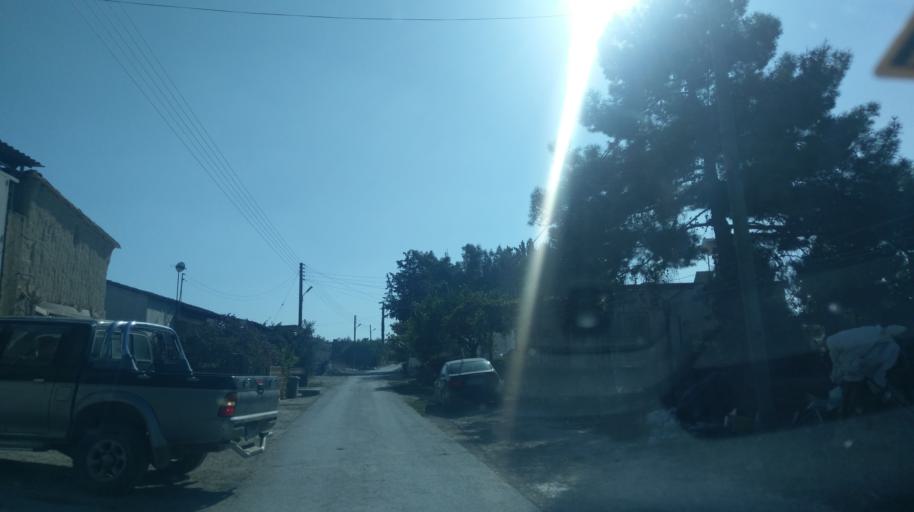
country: CY
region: Lefkosia
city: Lympia
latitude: 35.0075
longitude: 33.4643
